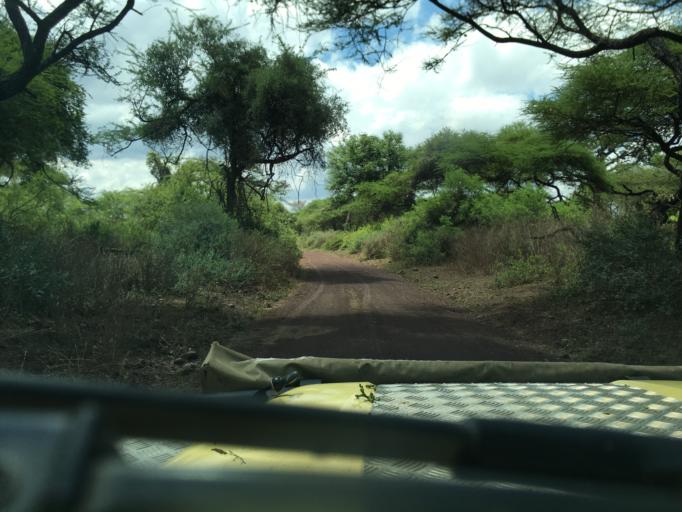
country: TZ
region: Arusha
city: Mto wa Mbu
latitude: -3.4212
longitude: 35.8143
